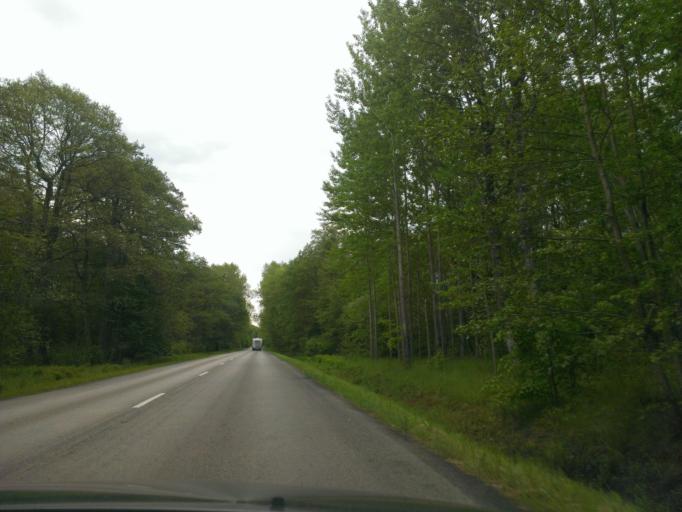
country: LT
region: Klaipedos apskritis
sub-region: Klaipeda
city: Palanga
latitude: 55.8693
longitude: 21.0739
